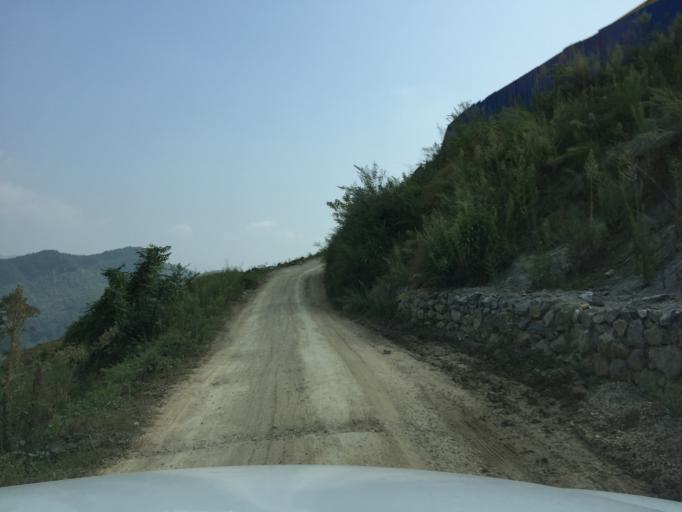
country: CN
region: Guizhou Sheng
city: Longquan
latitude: 28.2746
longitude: 108.0339
